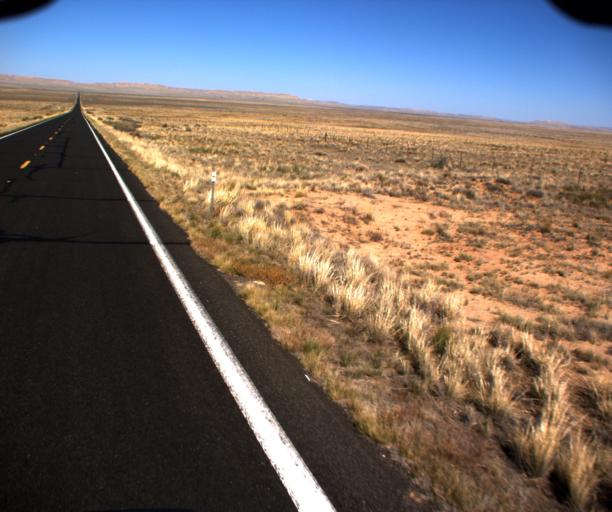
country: US
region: Arizona
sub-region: Navajo County
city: First Mesa
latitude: 35.6650
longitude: -110.4946
